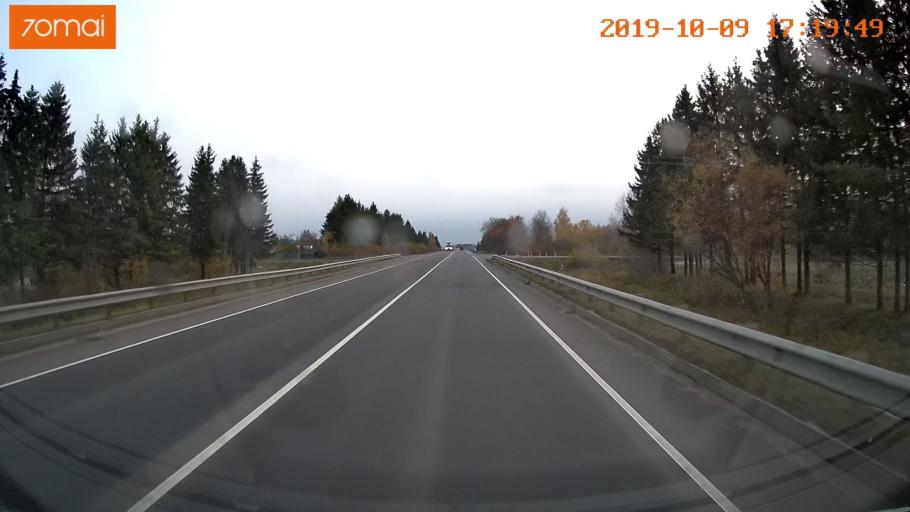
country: RU
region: Ivanovo
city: Furmanov
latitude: 57.2416
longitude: 41.1484
